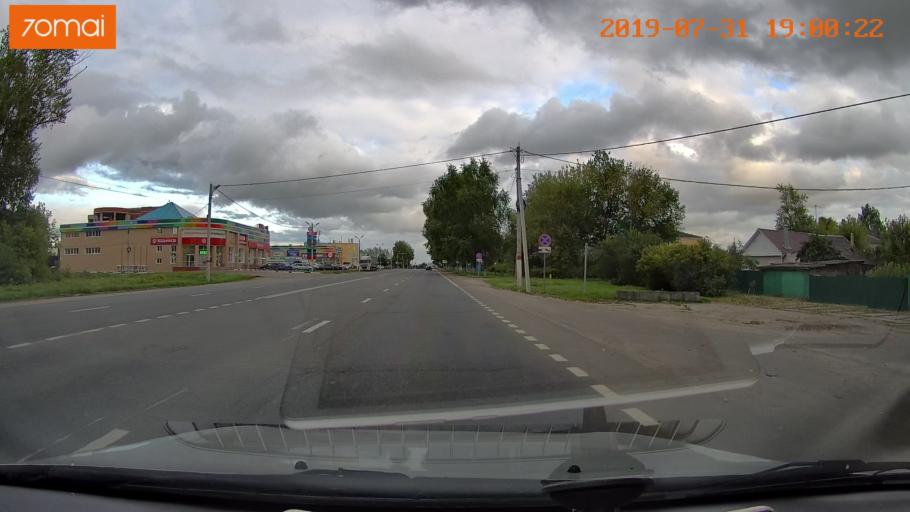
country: RU
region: Moskovskaya
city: Raduzhnyy
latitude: 55.1336
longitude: 38.7235
